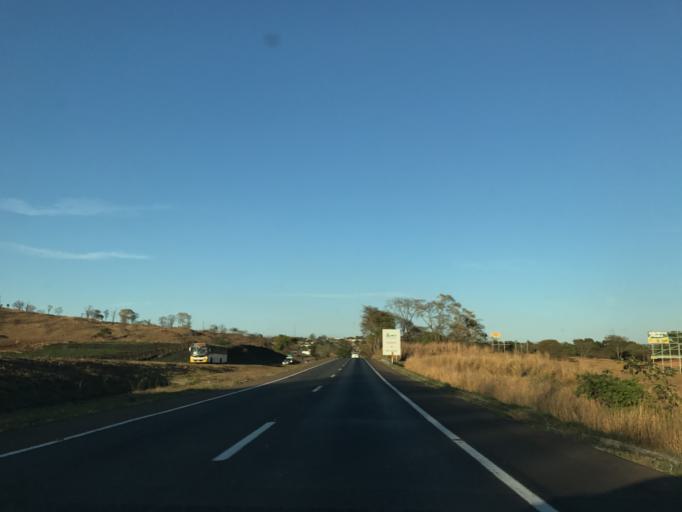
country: BR
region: Goias
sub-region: Goianapolis
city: Goianapolis
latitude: -16.4753
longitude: -49.0820
